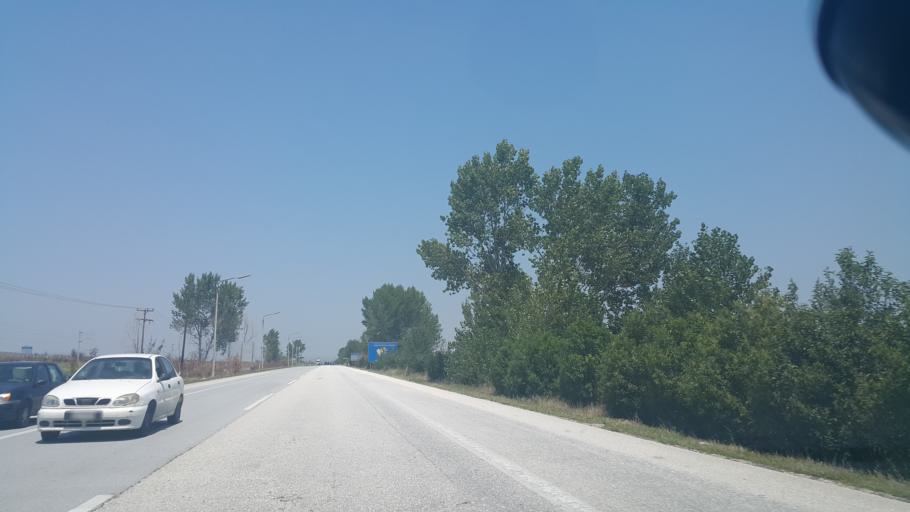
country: GR
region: Central Macedonia
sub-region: Nomos Thessalonikis
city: Prochoma
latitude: 40.8581
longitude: 22.6663
